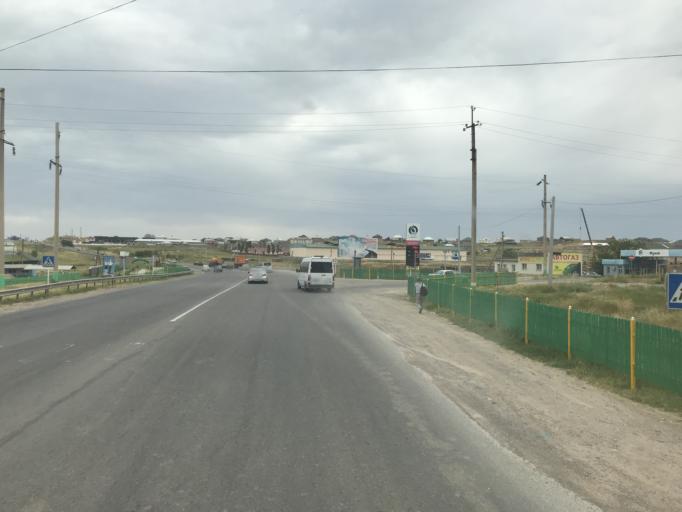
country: KZ
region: Ongtustik Qazaqstan
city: Saryaghash
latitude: 41.4761
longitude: 69.2063
